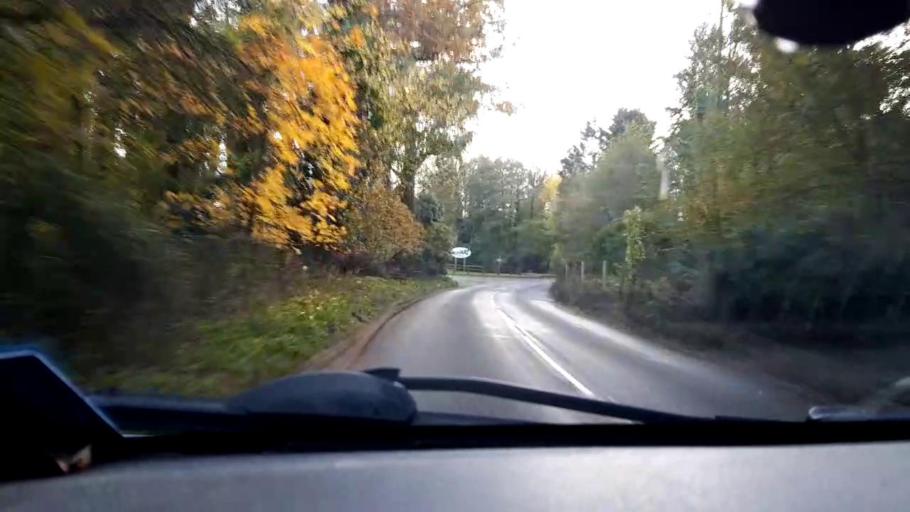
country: GB
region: England
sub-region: Norfolk
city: Mattishall
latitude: 52.7175
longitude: 1.1137
